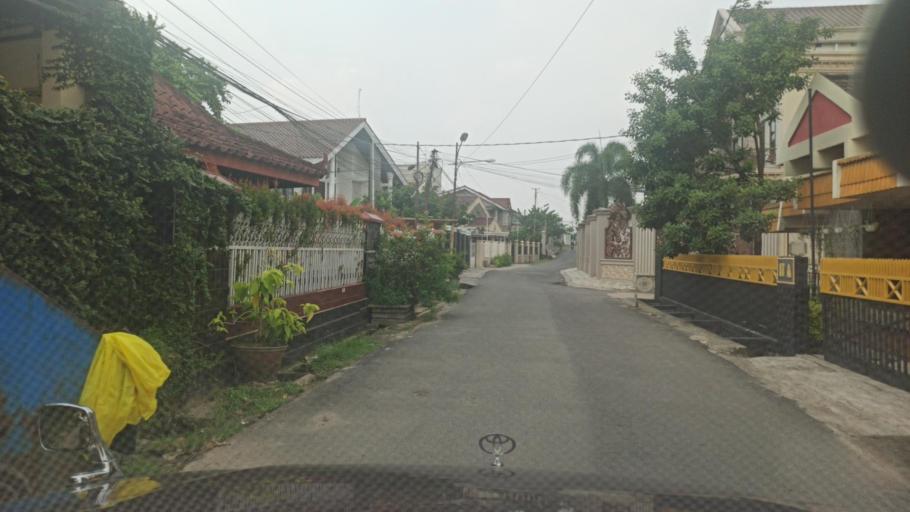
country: ID
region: South Sumatra
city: Plaju
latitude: -2.9922
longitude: 104.7412
